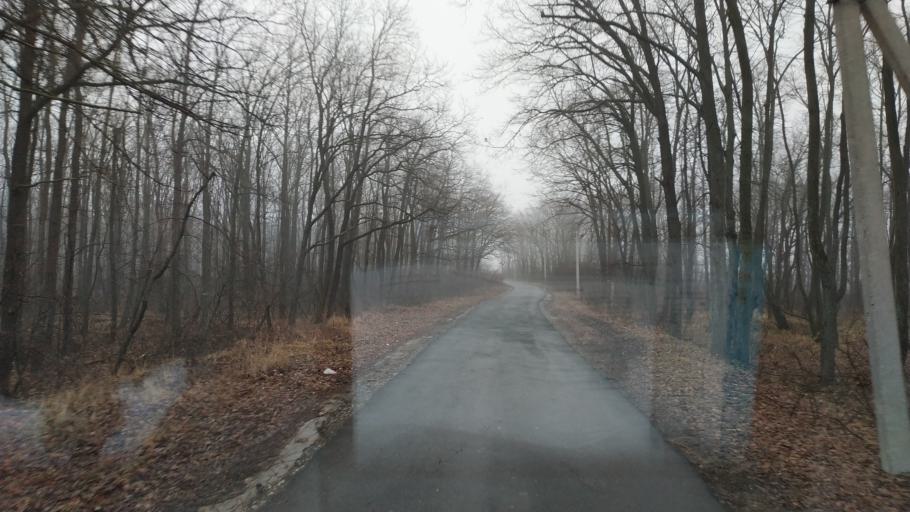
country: MD
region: Laloveni
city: Ialoveni
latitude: 46.9451
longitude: 28.7059
